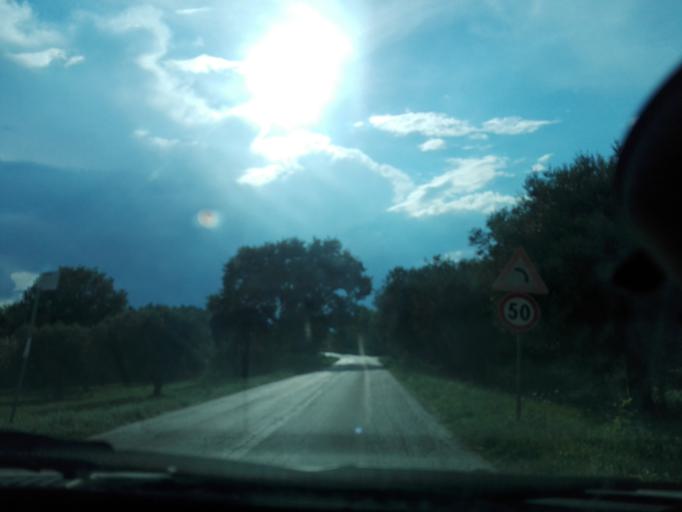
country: IT
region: Abruzzo
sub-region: Provincia di Pescara
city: Cappelle sul Tavo
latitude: 42.4559
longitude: 14.0952
